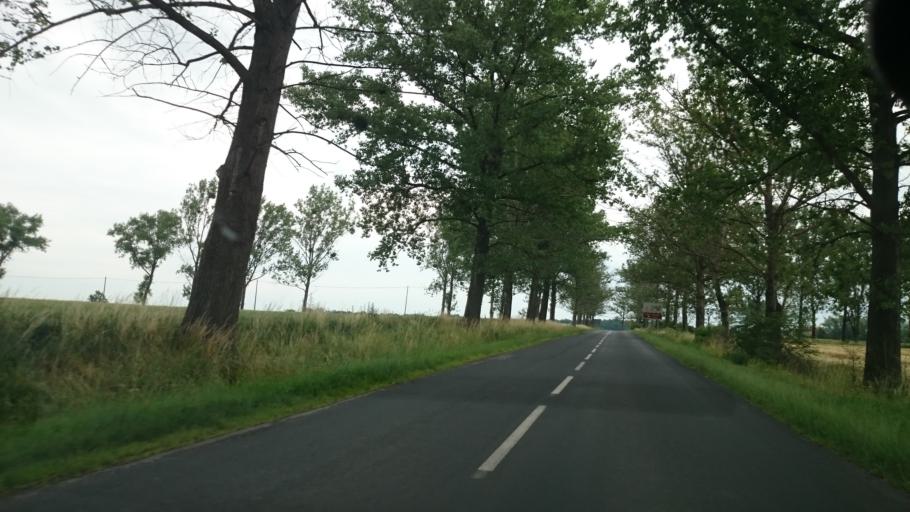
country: PL
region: Opole Voivodeship
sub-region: Powiat brzeski
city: Grodkow
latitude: 50.6778
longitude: 17.3156
